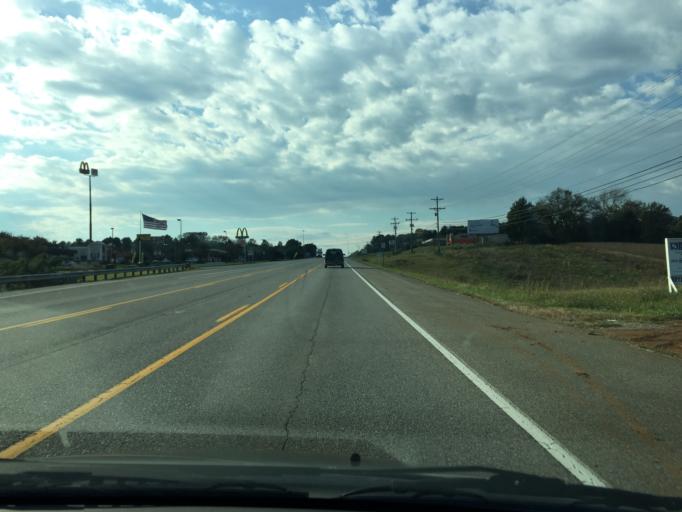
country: US
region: Tennessee
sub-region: Loudon County
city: Loudon
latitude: 35.7309
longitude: -84.3866
